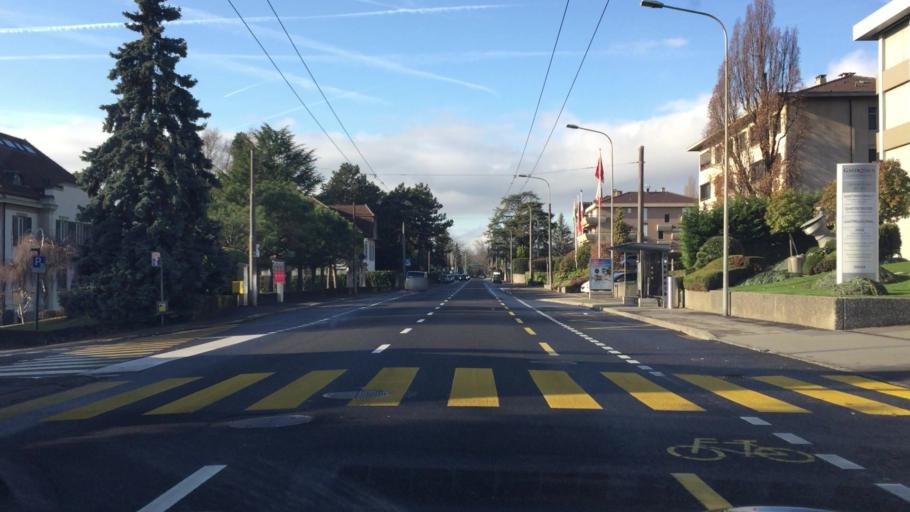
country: CH
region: Vaud
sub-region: Lavaux-Oron District
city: Pully
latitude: 46.5066
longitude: 6.6499
